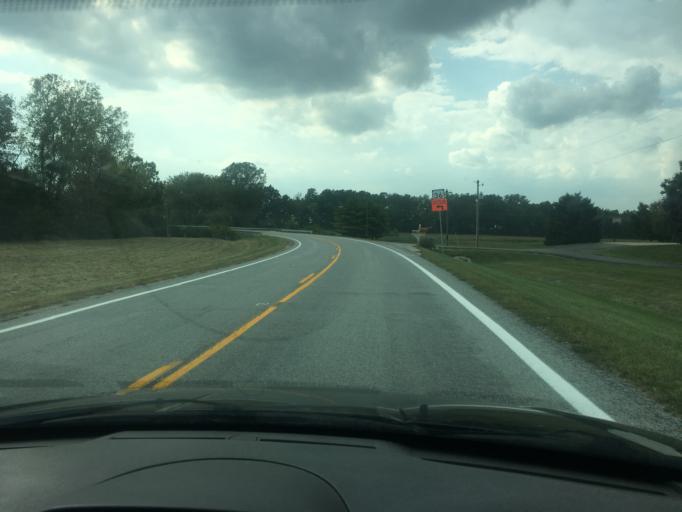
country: US
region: Ohio
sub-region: Champaign County
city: Urbana
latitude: 40.1576
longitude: -83.7824
